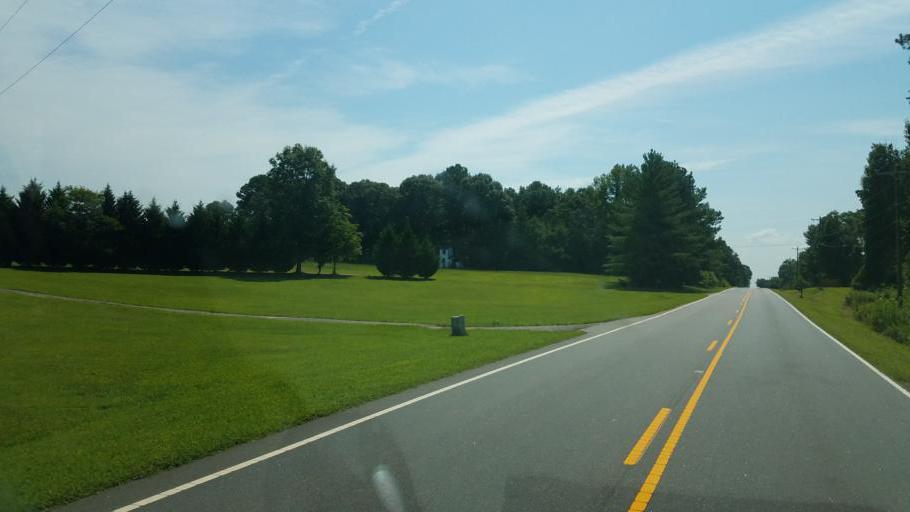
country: US
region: North Carolina
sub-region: Gaston County
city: Cherryville
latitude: 35.5144
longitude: -81.4692
